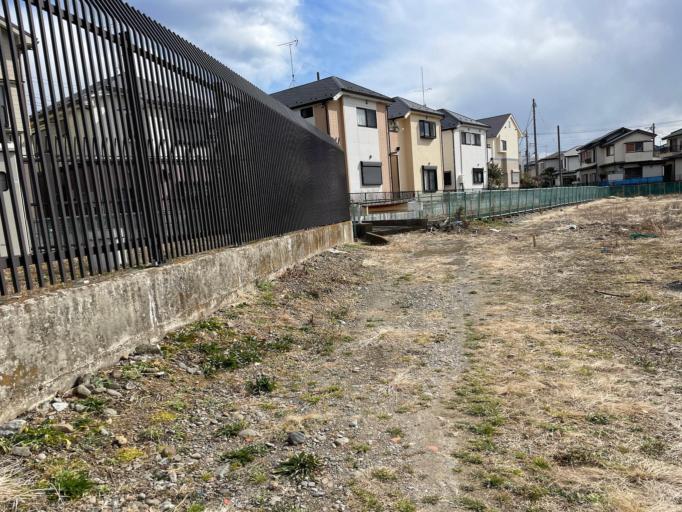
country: JP
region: Tokyo
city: Chofugaoka
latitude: 35.6544
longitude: 139.5223
